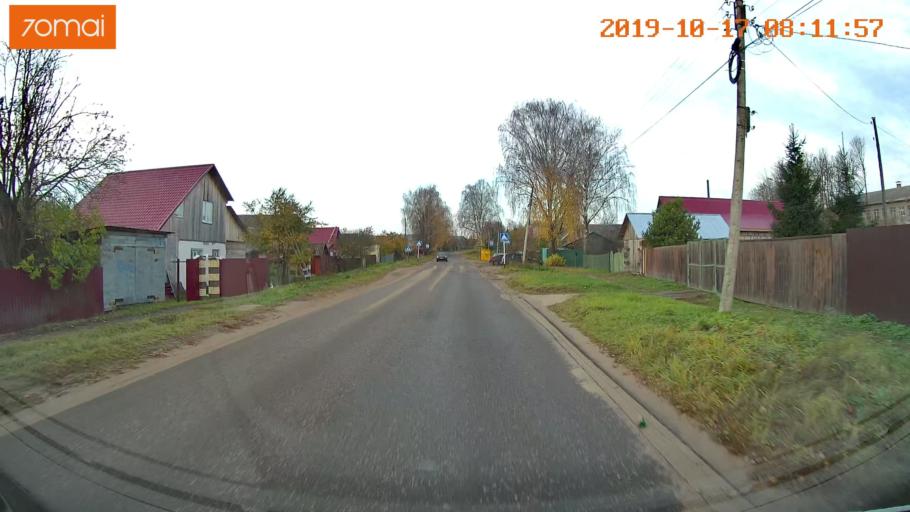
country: RU
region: Vladimir
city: Kol'chugino
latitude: 56.3005
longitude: 39.3628
